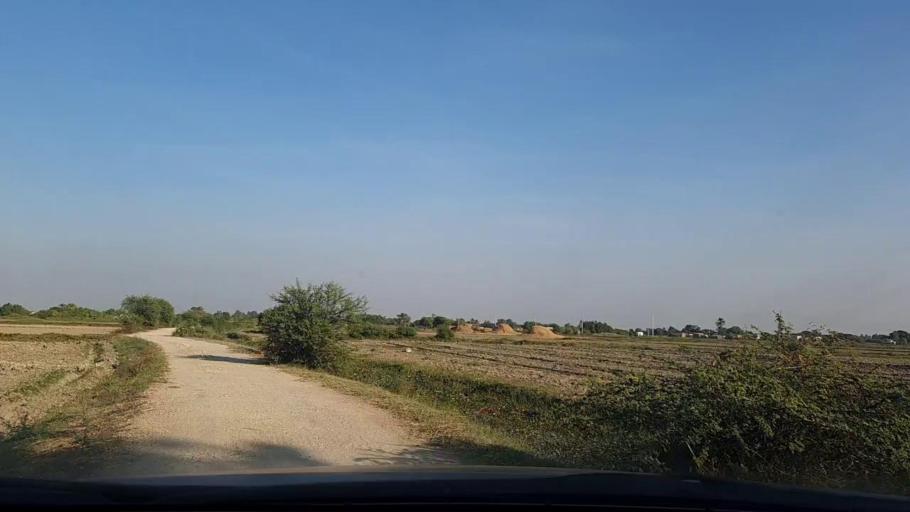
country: PK
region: Sindh
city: Mirpur Sakro
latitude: 24.5161
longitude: 67.6421
